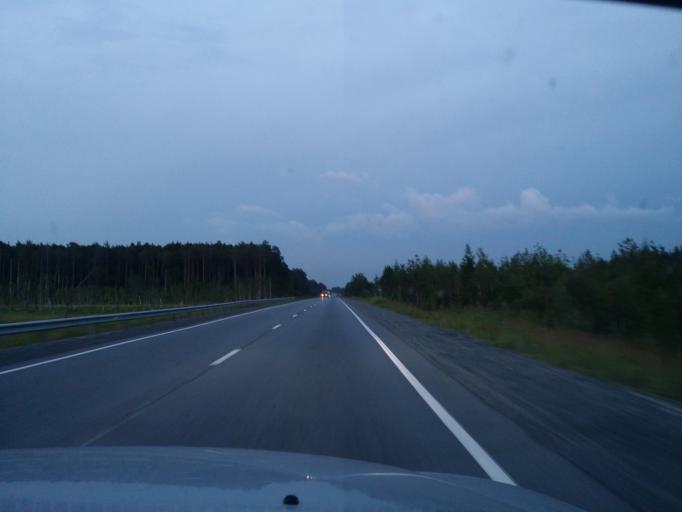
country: RU
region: Khanty-Mansiyskiy Avtonomnyy Okrug
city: Surgut
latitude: 61.3579
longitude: 73.3640
